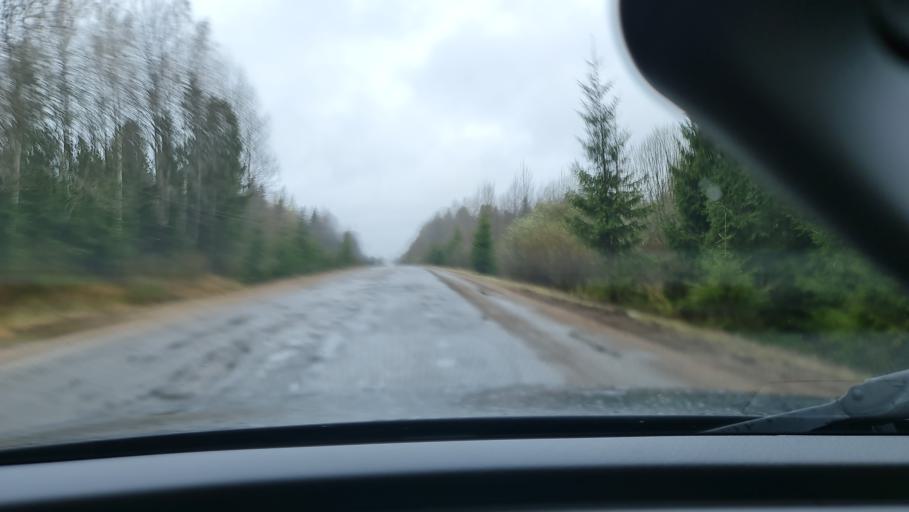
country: RU
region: Novgorod
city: Kresttsy
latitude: 58.0298
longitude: 32.8138
